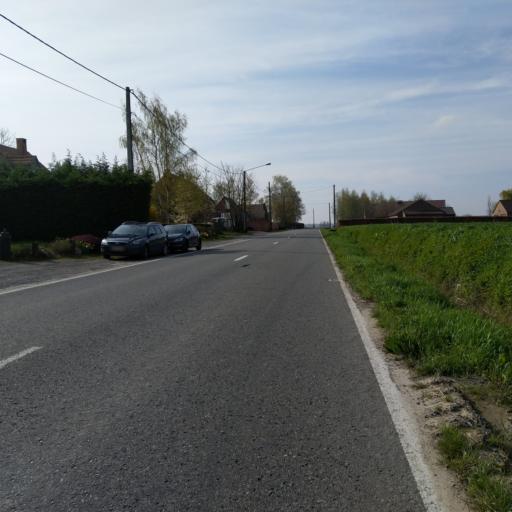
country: BE
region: Wallonia
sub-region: Province du Hainaut
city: Quevy-le-Petit
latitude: 50.3559
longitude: 3.8892
